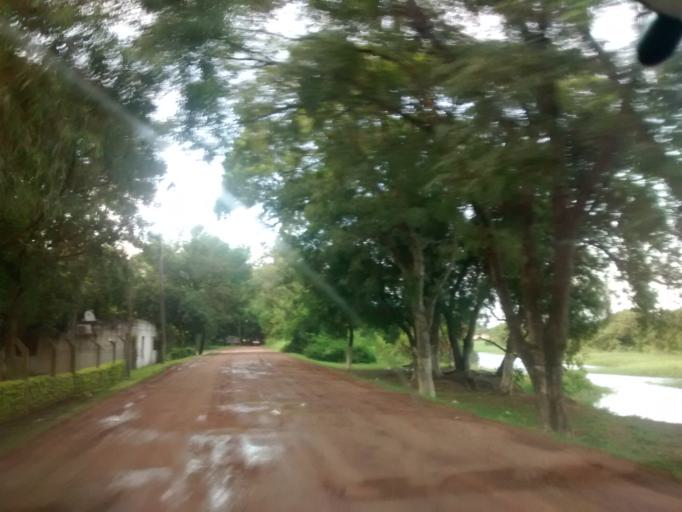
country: AR
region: Chaco
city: Fontana
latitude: -27.4204
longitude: -59.0058
